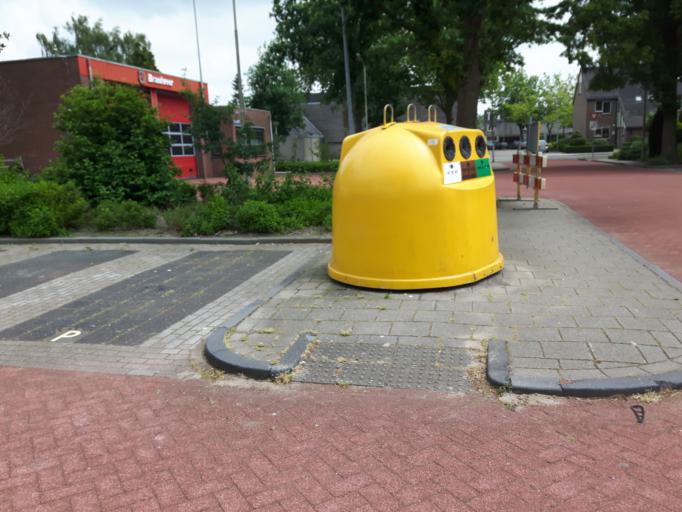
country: NL
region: South Holland
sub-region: Gemeente Krimpen aan den IJssel
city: Krimpen aan den IJssel
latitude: 51.9344
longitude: 4.6340
